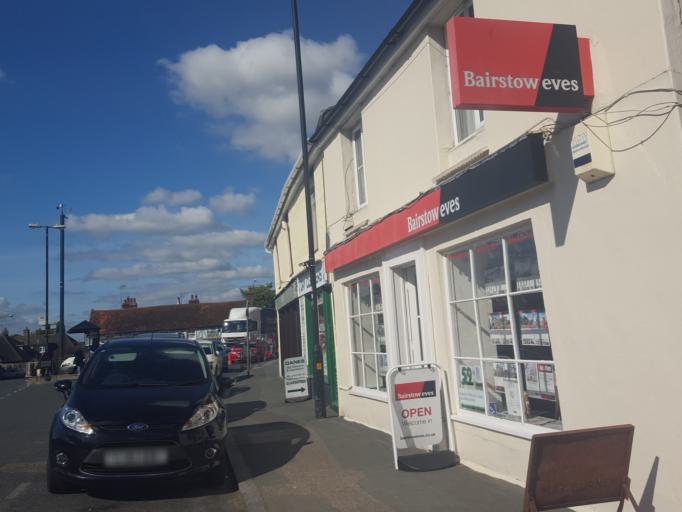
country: GB
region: England
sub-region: Essex
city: Brightlingsea
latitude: 51.8110
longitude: 1.0254
